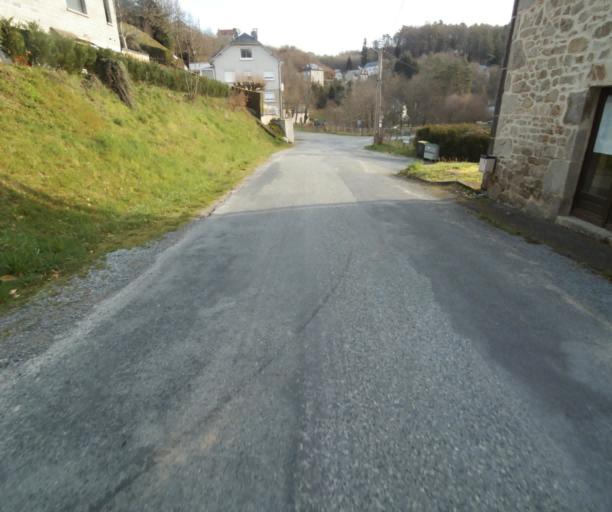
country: FR
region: Limousin
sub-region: Departement de la Correze
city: Correze
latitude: 45.3719
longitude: 1.8796
